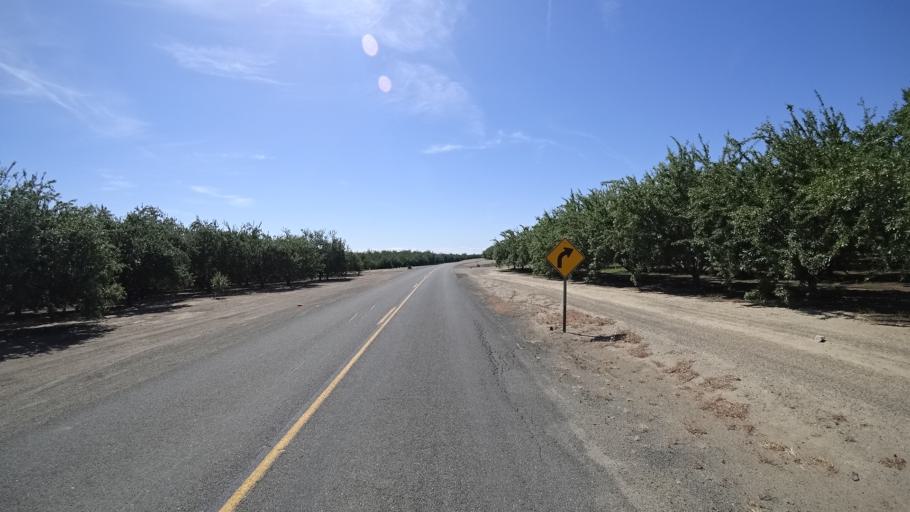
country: US
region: California
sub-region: Kings County
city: Kettleman City
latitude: 35.9643
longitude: -119.9377
